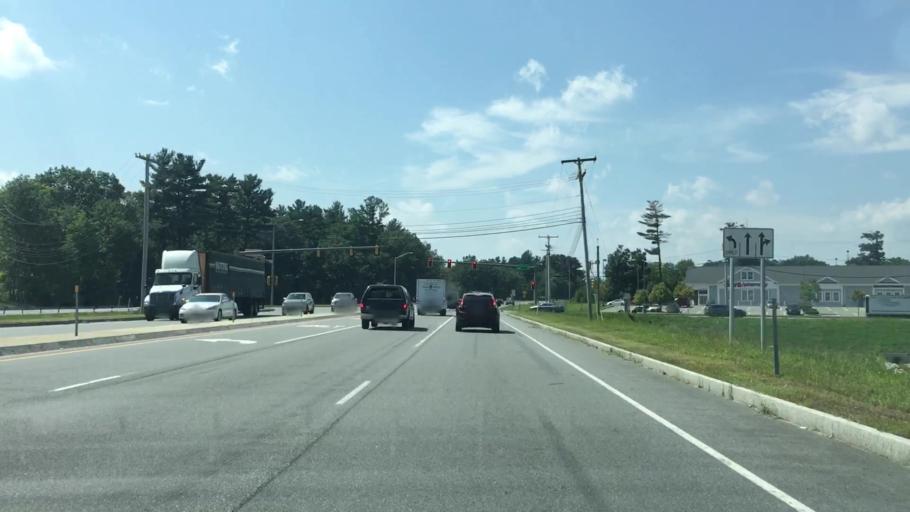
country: US
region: New Hampshire
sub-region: Rockingham County
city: Windham
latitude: 42.8074
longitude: -71.2860
